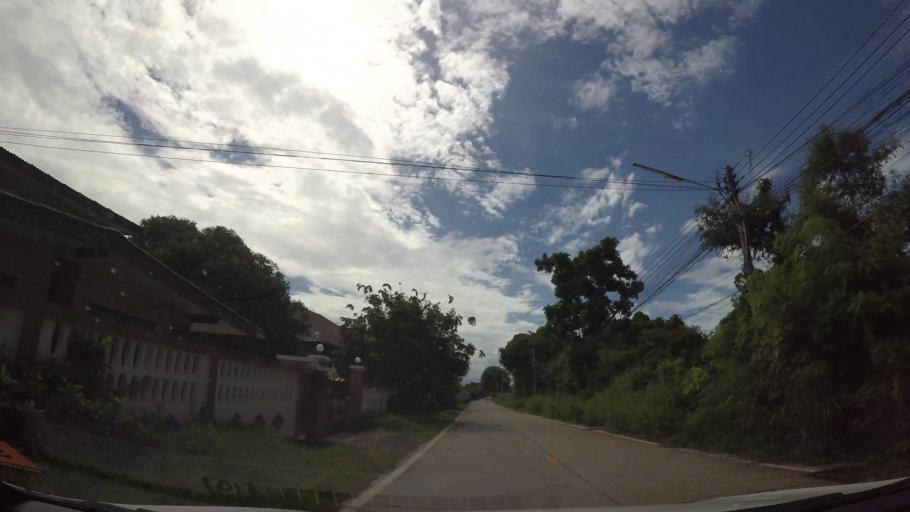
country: TH
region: Rayong
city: Rayong
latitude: 12.6672
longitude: 101.2893
